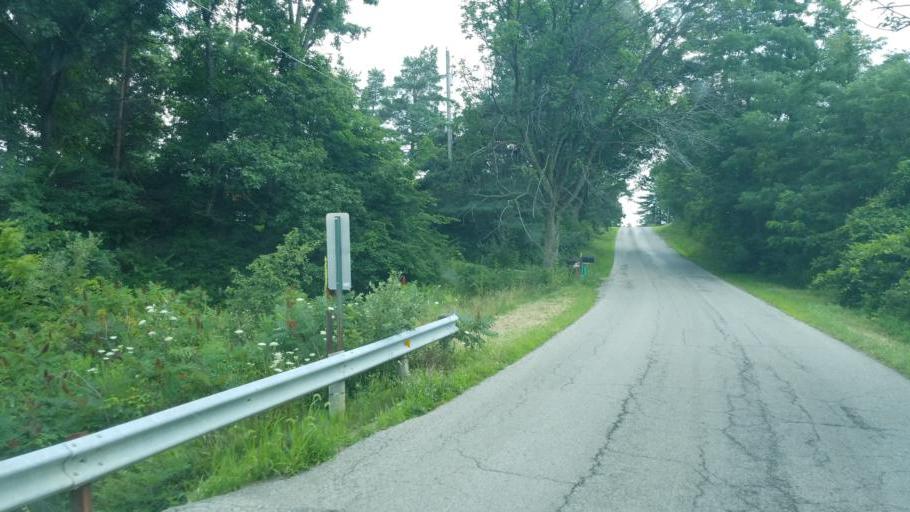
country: US
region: Ohio
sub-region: Richland County
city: Ontario
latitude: 40.8044
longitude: -82.6167
